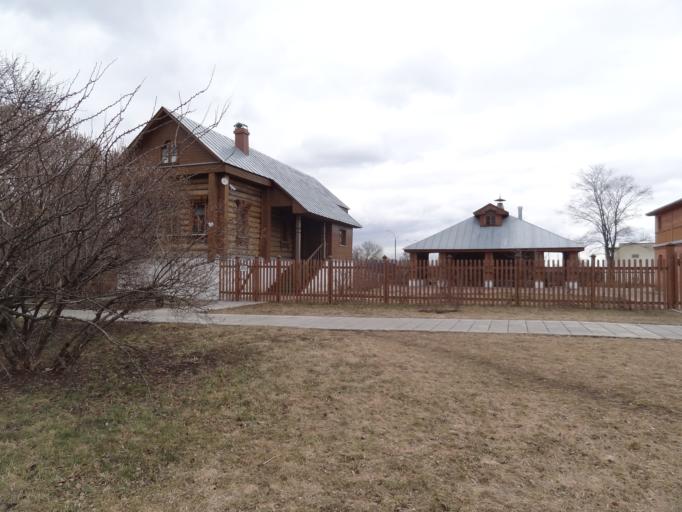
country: RU
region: Moscow
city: Kolomenskoye
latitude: 55.6749
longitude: 37.6708
